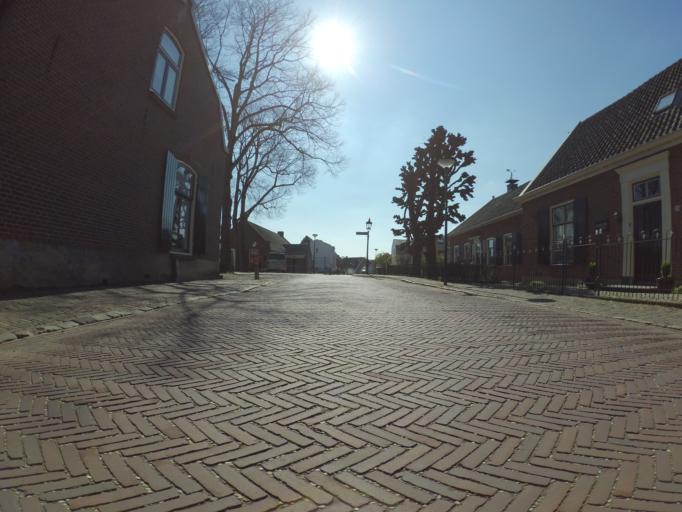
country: NL
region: Utrecht
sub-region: Gemeente Utrechtse Heuvelrug
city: Driebergen-Rijsenburg
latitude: 52.0242
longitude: 5.2448
